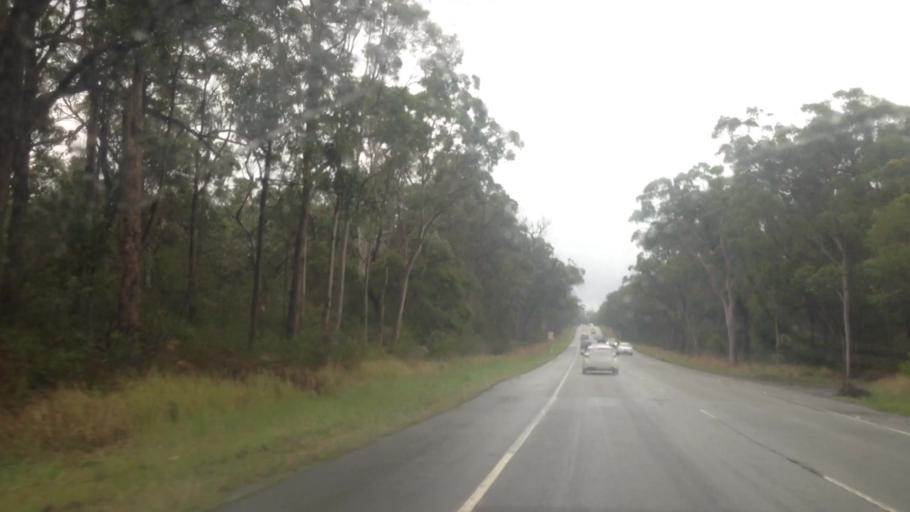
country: AU
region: New South Wales
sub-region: Lake Macquarie Shire
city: Dora Creek
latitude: -33.1345
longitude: 151.4770
